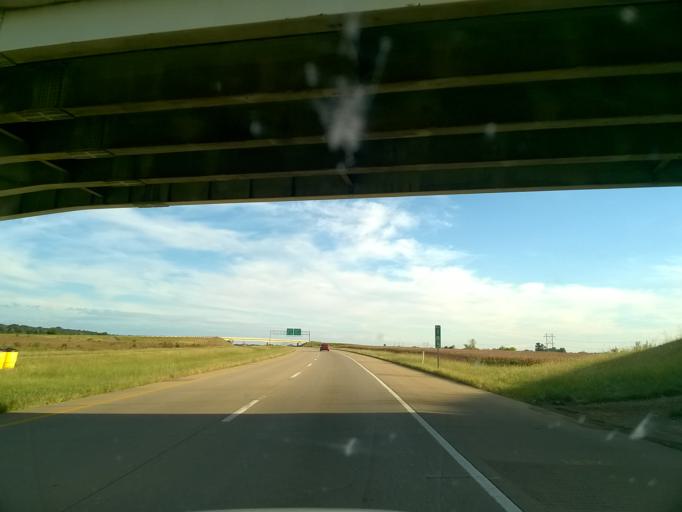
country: US
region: Indiana
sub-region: Vanderburgh County
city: Darmstadt
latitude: 38.1353
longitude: -87.4729
